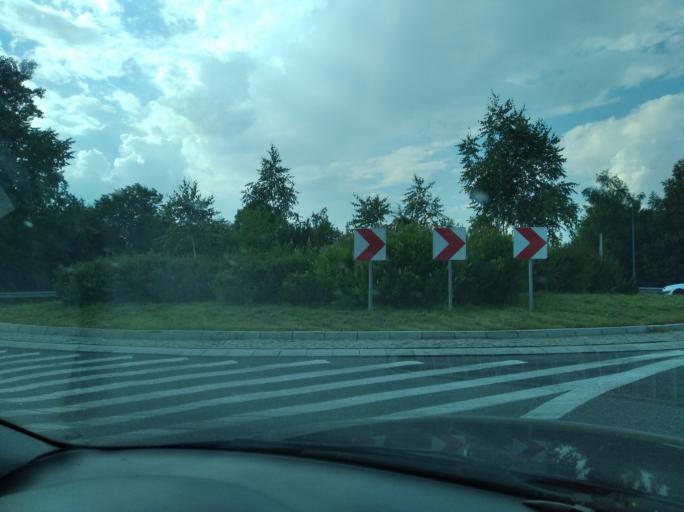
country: PL
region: Subcarpathian Voivodeship
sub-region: Powiat rzeszowski
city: Rudna Mala
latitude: 50.1084
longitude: 21.9757
